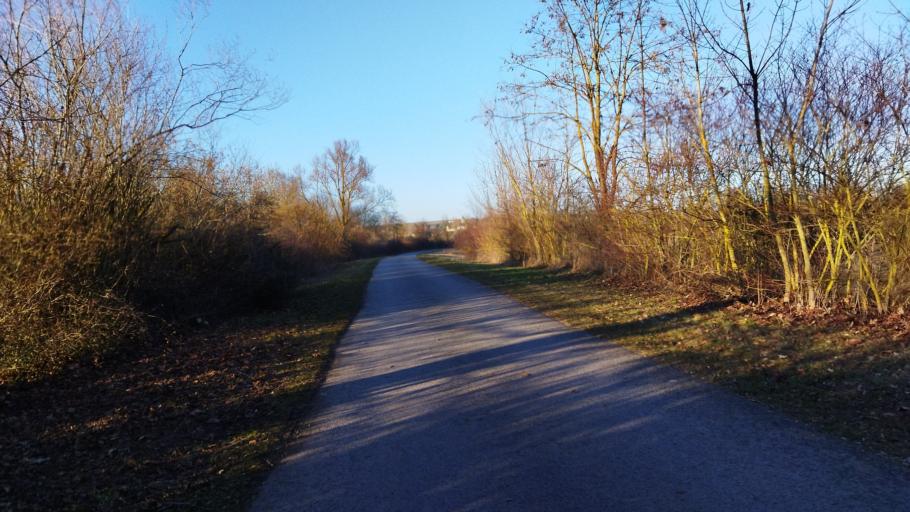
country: DE
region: Bavaria
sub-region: Regierungsbezirk Unterfranken
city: Mainstockheim
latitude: 49.7903
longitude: 10.1565
